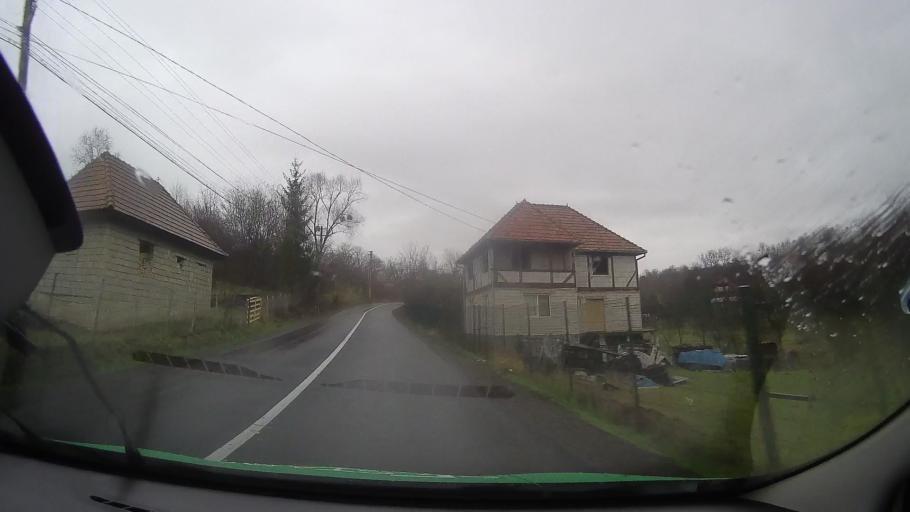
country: RO
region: Mures
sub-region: Comuna Vatava
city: Vatava
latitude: 46.9534
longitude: 24.7630
